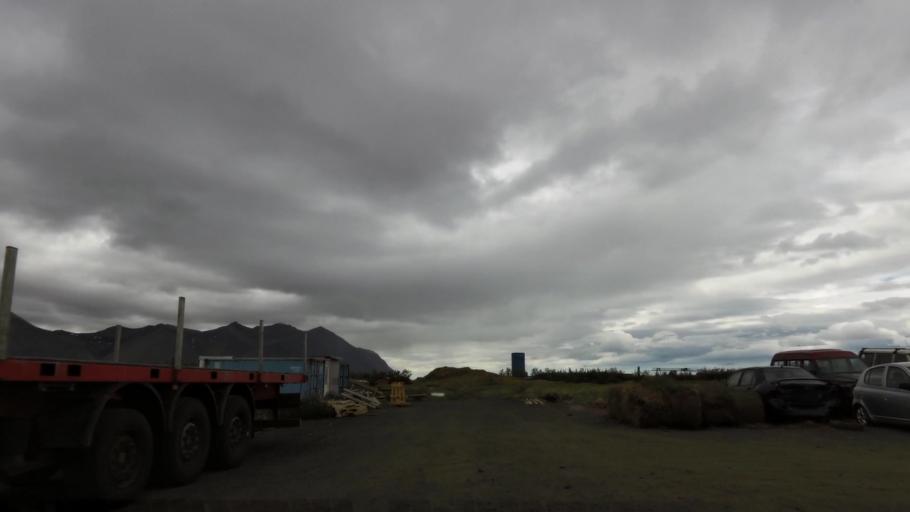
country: IS
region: West
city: Borgarnes
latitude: 64.5659
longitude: -21.8963
